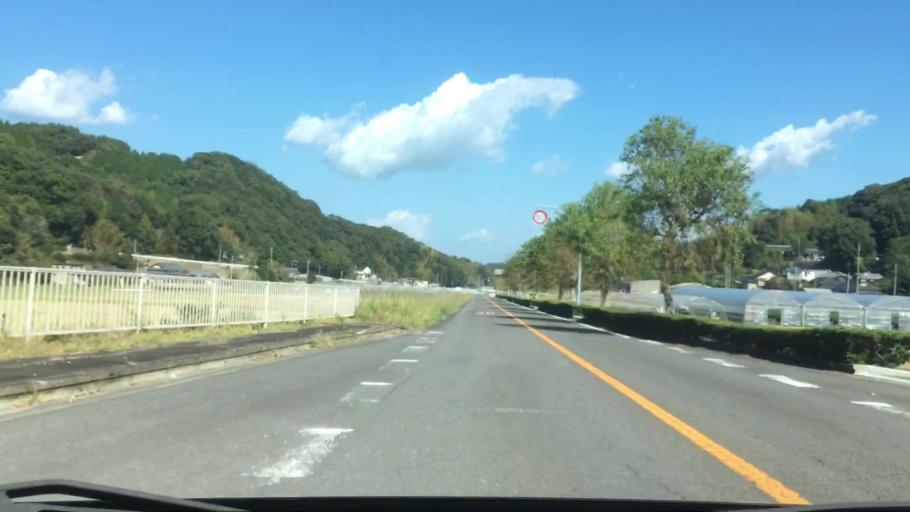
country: JP
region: Nagasaki
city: Sasebo
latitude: 32.9593
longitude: 129.6444
